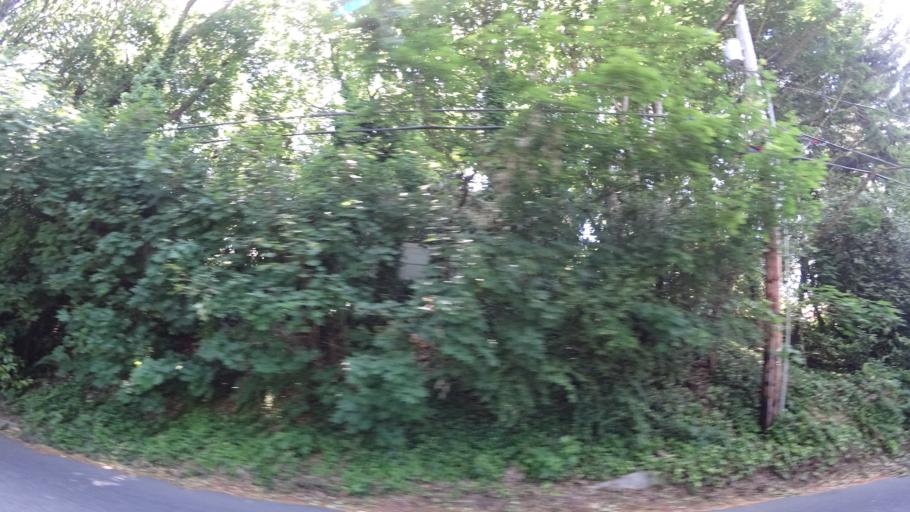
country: US
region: Oregon
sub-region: Washington County
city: Garden Home-Whitford
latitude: 45.4731
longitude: -122.7077
